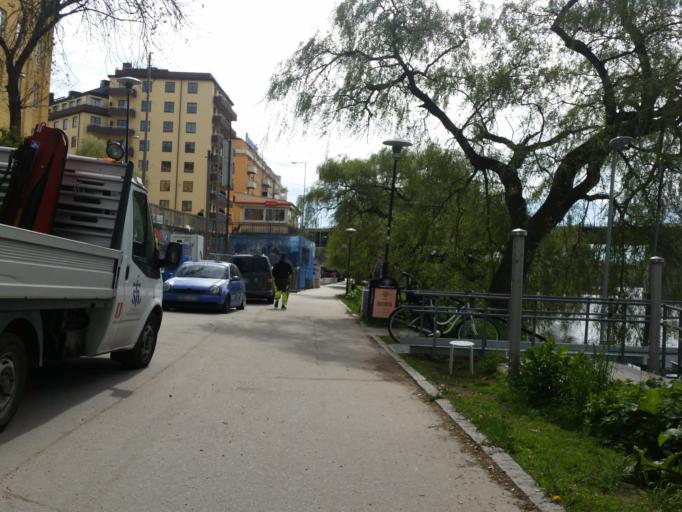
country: SE
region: Stockholm
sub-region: Stockholms Kommun
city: Arsta
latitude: 59.3152
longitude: 18.0301
